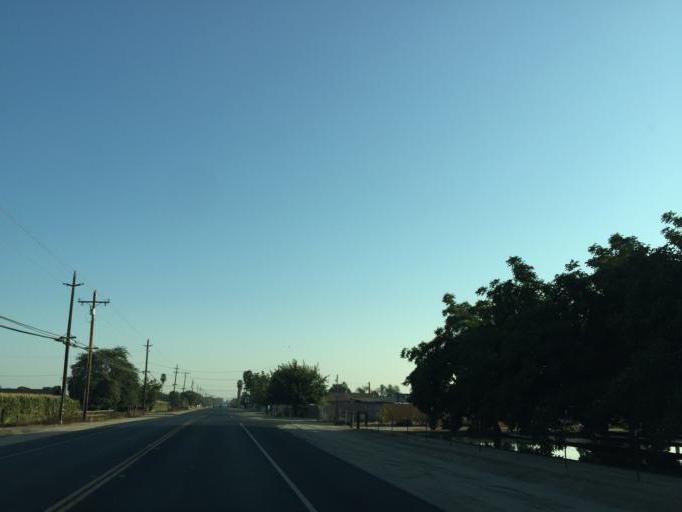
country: US
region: California
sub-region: Tulare County
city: Visalia
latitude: 36.3777
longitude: -119.2968
